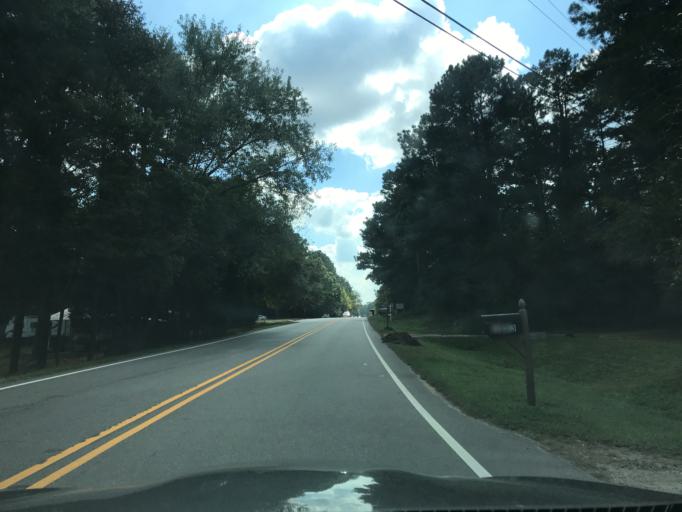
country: US
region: North Carolina
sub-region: Wake County
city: Wake Forest
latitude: 35.9465
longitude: -78.5295
